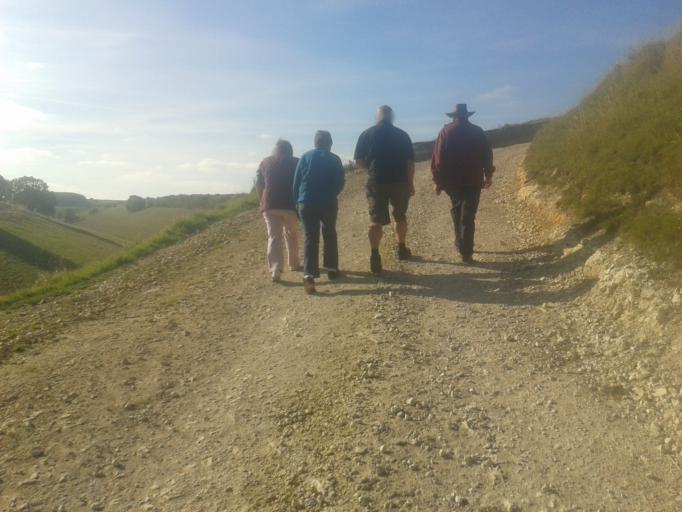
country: GB
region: England
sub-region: North Yorkshire
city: Thixendale
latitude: 54.0402
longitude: -0.7206
